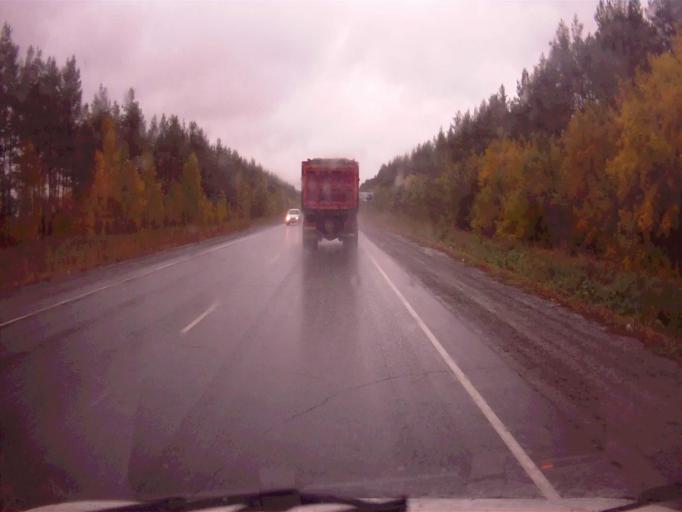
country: RU
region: Chelyabinsk
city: Roshchino
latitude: 55.3588
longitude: 61.2305
